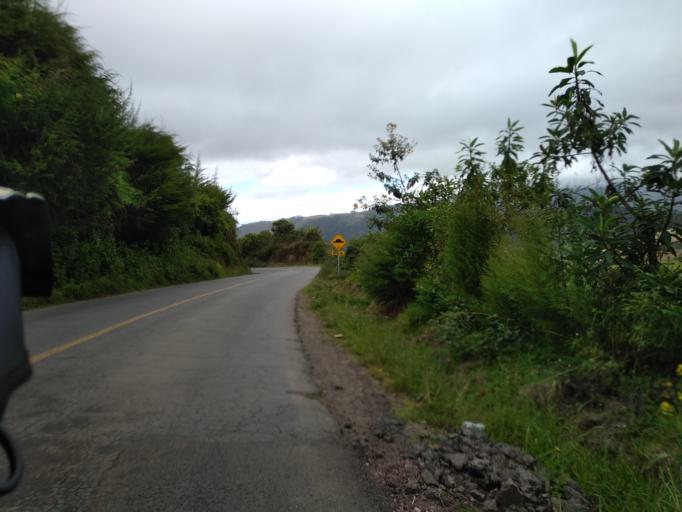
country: EC
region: Carchi
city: El Angel
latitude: 0.6303
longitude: -77.9311
